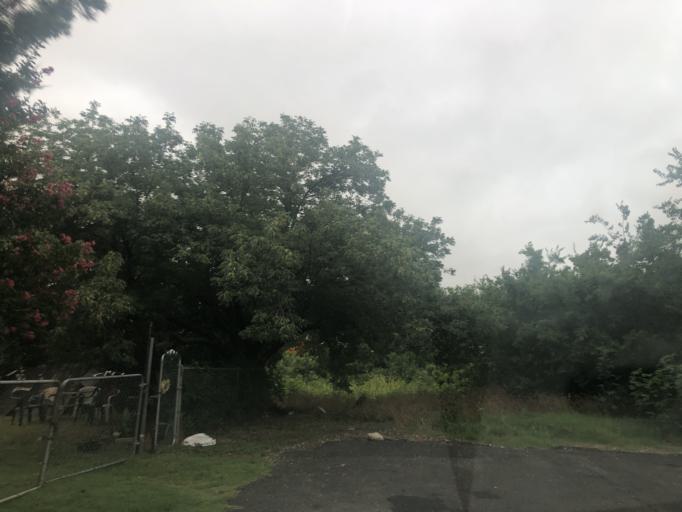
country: US
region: Texas
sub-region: Dallas County
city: Cockrell Hill
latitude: 32.7768
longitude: -96.8672
